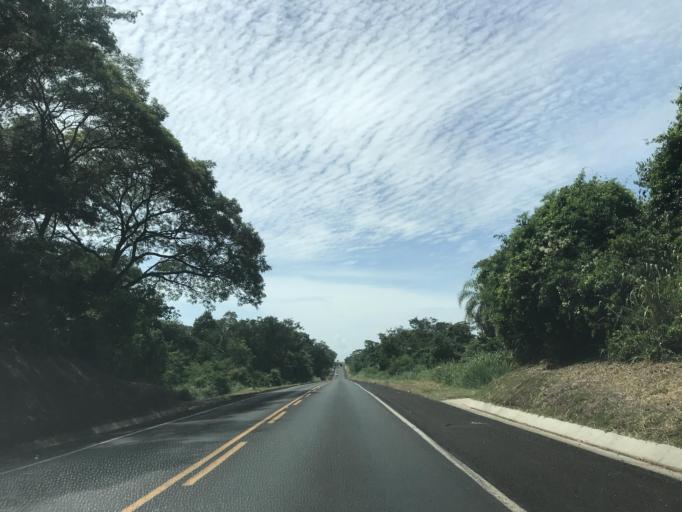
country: BR
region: Parana
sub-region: Paranavai
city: Paranavai
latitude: -23.0202
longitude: -52.5002
